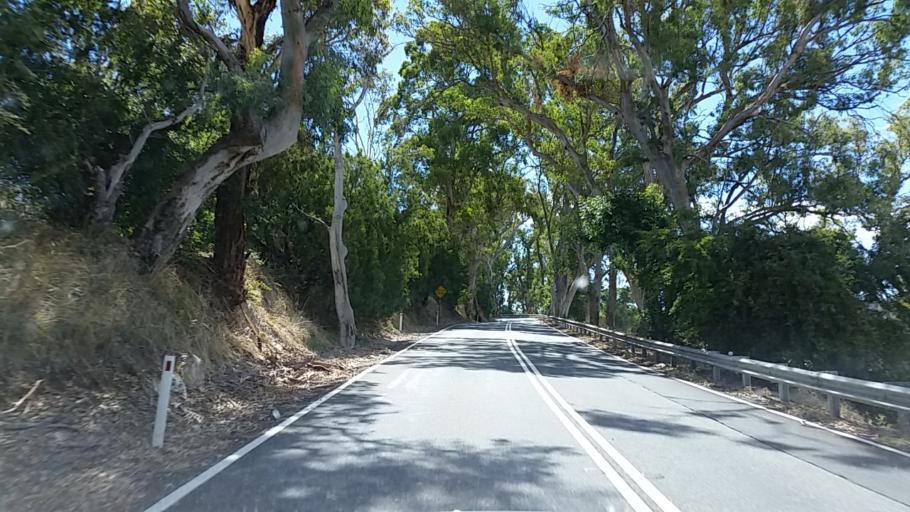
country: AU
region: South Australia
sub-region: Adelaide Hills
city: Gumeracha
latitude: -34.8203
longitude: 138.9047
